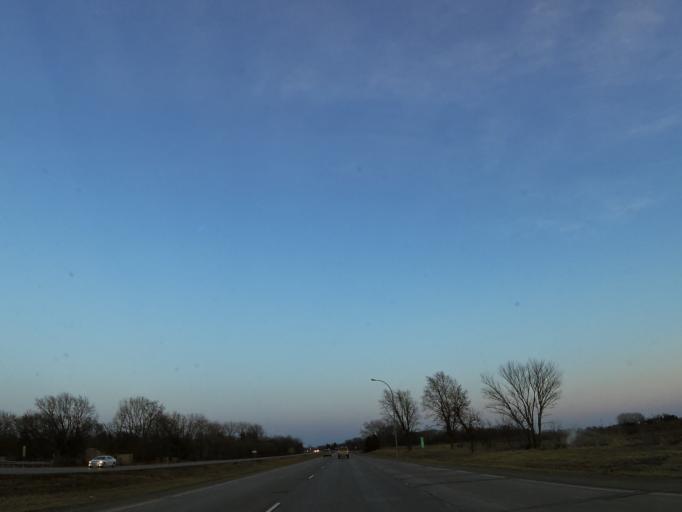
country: US
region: Minnesota
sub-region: Mower County
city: Austin
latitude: 43.6733
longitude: -92.9262
